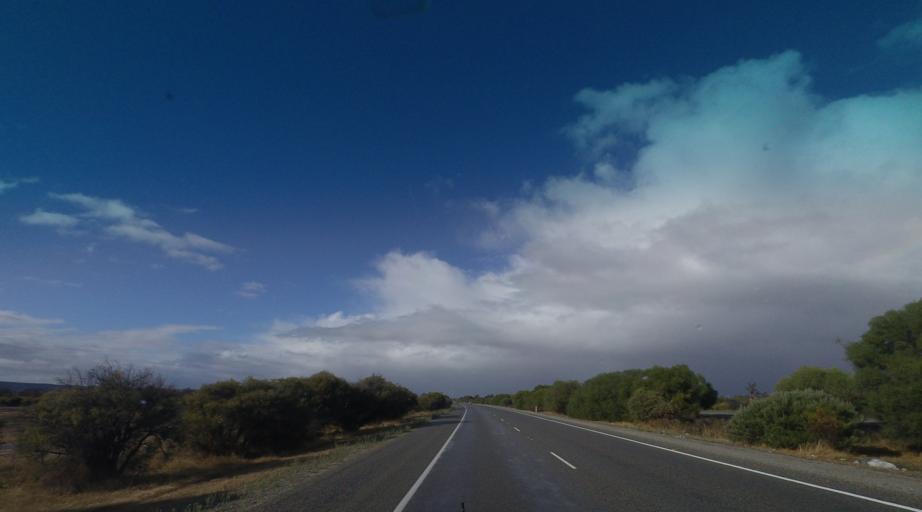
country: AU
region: Western Australia
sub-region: Serpentine-Jarrahdale
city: Oakford
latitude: -32.1721
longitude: 115.9609
